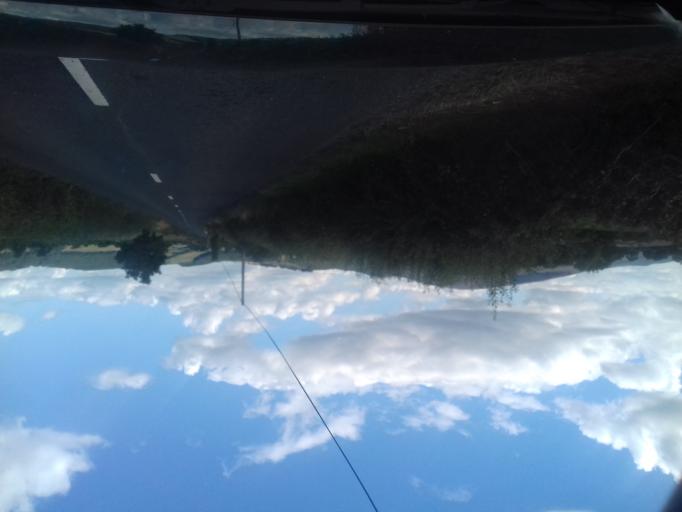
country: IE
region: Munster
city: Carrick-on-Suir
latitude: 52.3757
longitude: -7.4520
